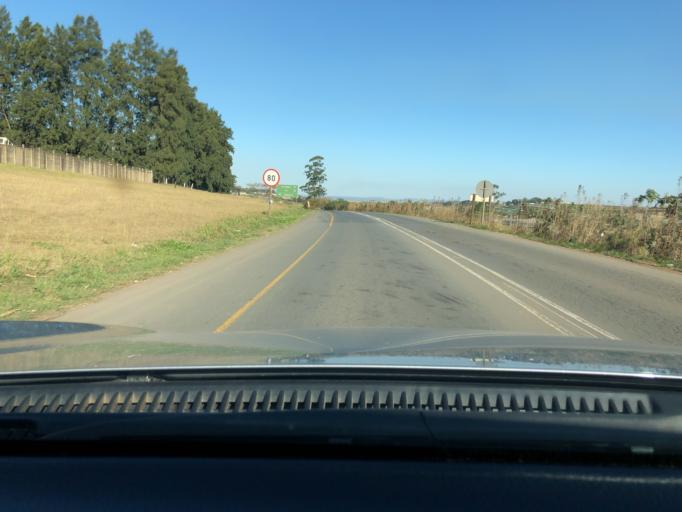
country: ZA
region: KwaZulu-Natal
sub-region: uMgungundlovu District Municipality
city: Camperdown
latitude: -29.7277
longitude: 30.5007
